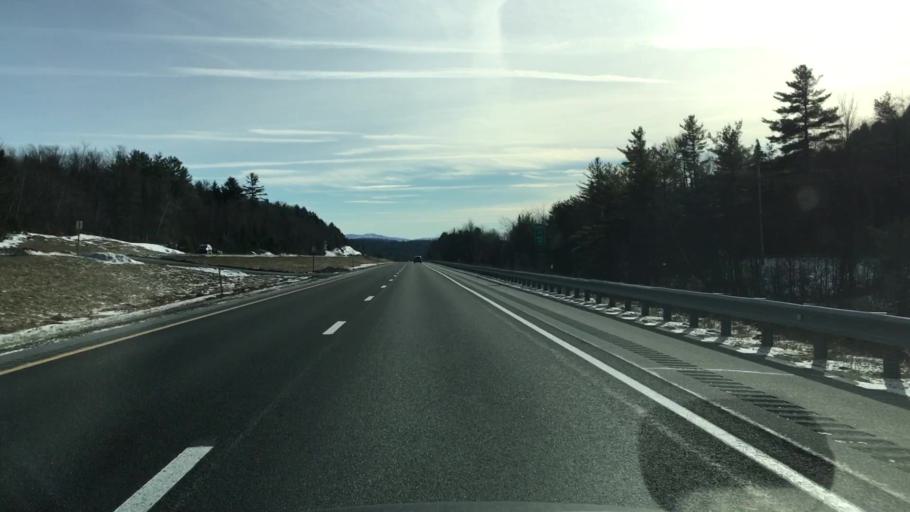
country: US
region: New Hampshire
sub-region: Sullivan County
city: Grantham
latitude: 43.5552
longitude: -72.1415
